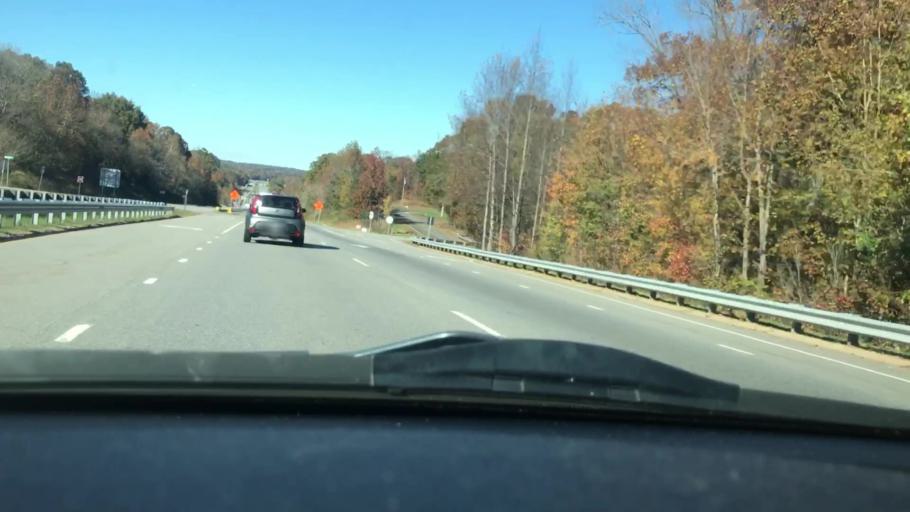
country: US
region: North Carolina
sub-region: Rockingham County
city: Stoneville
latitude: 36.4314
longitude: -79.9296
